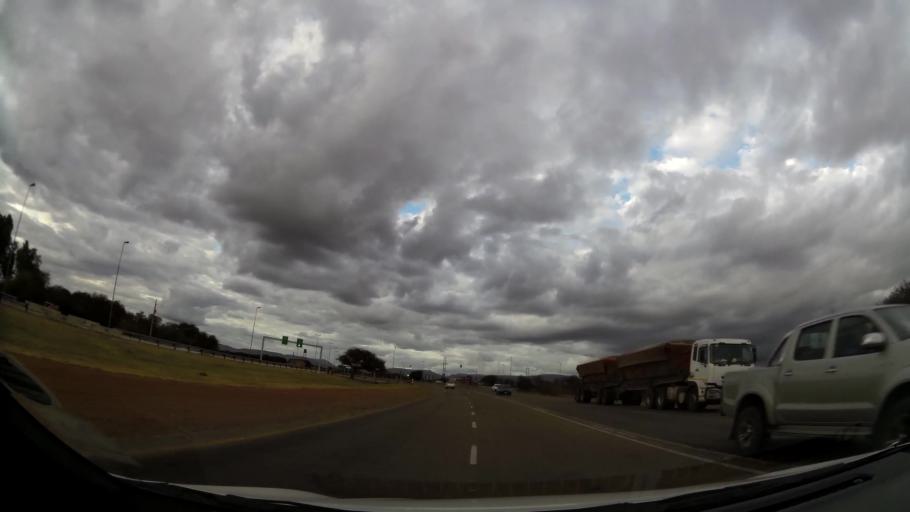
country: ZA
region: Limpopo
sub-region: Waterberg District Municipality
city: Mokopane
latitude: -24.2747
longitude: 28.9782
